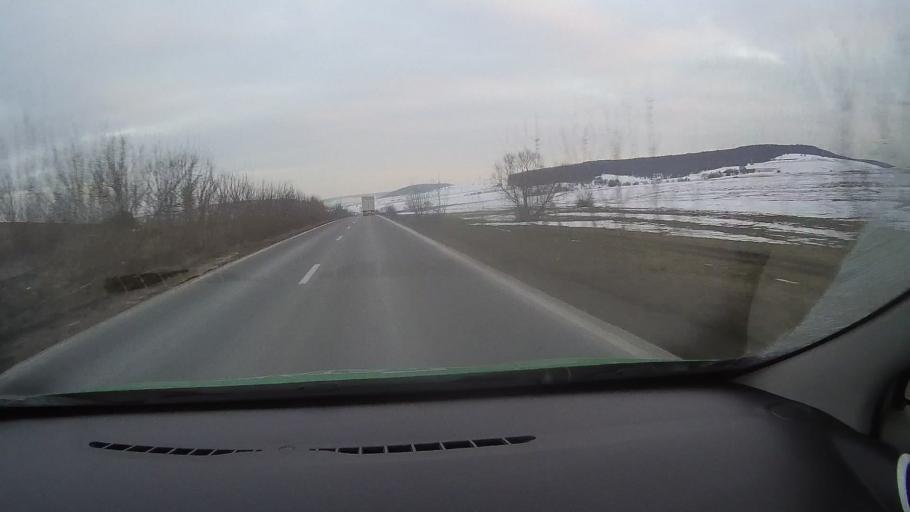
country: RO
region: Harghita
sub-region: Comuna Lupeni
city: Lupeni
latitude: 46.3576
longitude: 25.2509
